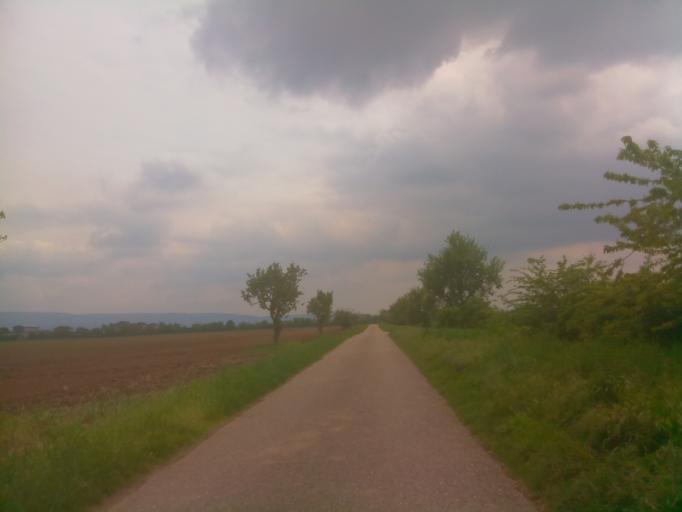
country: DE
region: Baden-Wuerttemberg
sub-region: Karlsruhe Region
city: Plankstadt
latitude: 49.4095
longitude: 8.5749
